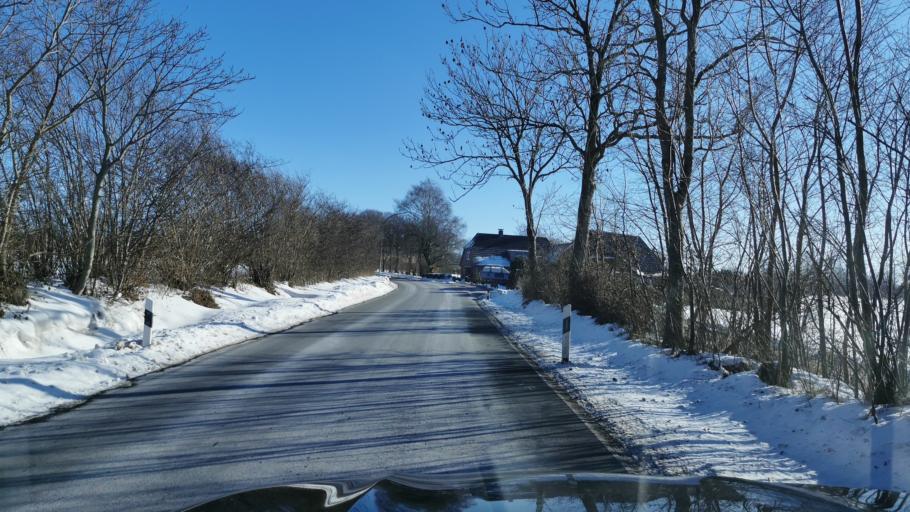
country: DE
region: Schleswig-Holstein
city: Sorup
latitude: 54.7313
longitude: 9.6509
